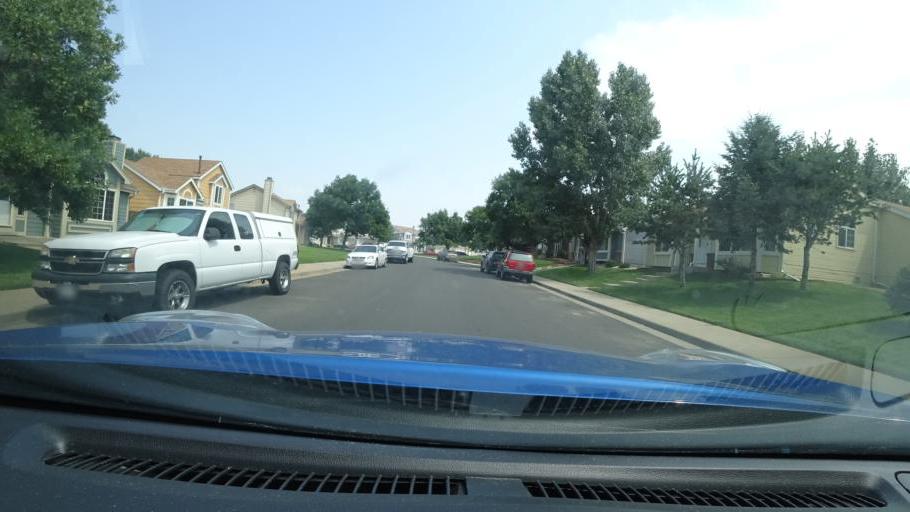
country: US
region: Colorado
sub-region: Adams County
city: Aurora
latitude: 39.7756
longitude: -104.7409
